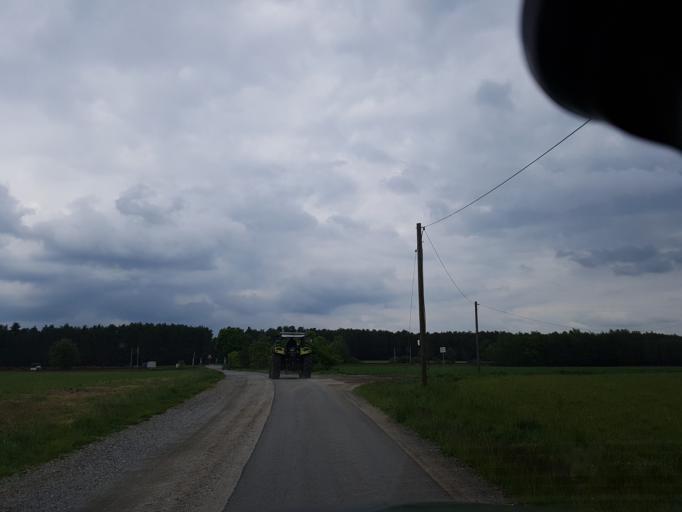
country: DE
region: Brandenburg
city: Crinitz
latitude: 51.6610
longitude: 13.7855
